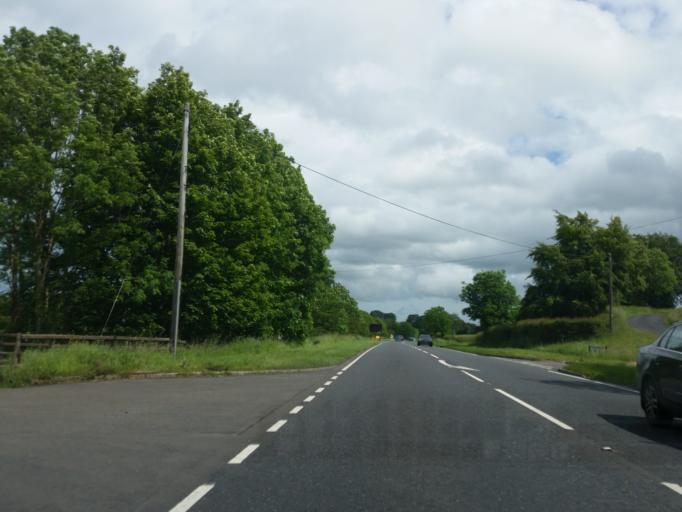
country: IE
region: Ulster
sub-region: County Monaghan
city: Monaghan
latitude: 54.4738
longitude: -7.0630
